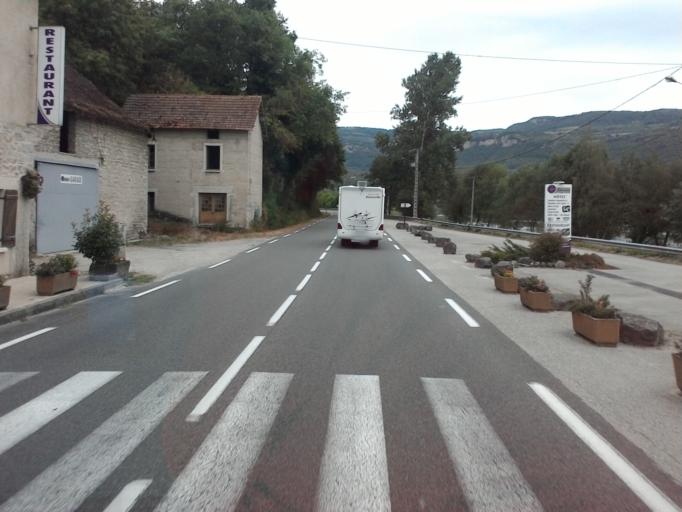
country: FR
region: Rhone-Alpes
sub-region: Departement de l'Ain
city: Sault-Brenaz
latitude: 45.8424
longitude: 5.4156
